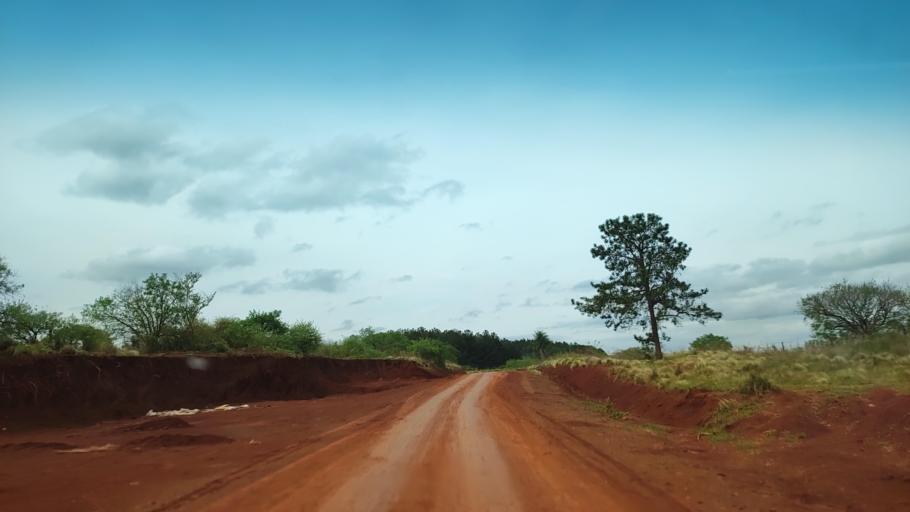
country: AR
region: Misiones
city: Garupa
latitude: -27.5160
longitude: -55.9727
